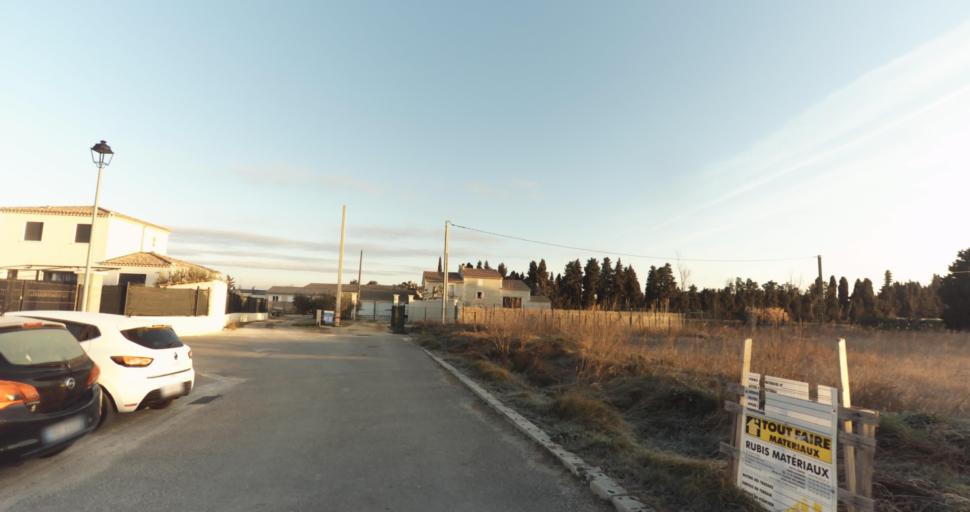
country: FR
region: Provence-Alpes-Cote d'Azur
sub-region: Departement des Bouches-du-Rhone
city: Barbentane
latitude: 43.9014
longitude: 4.7651
